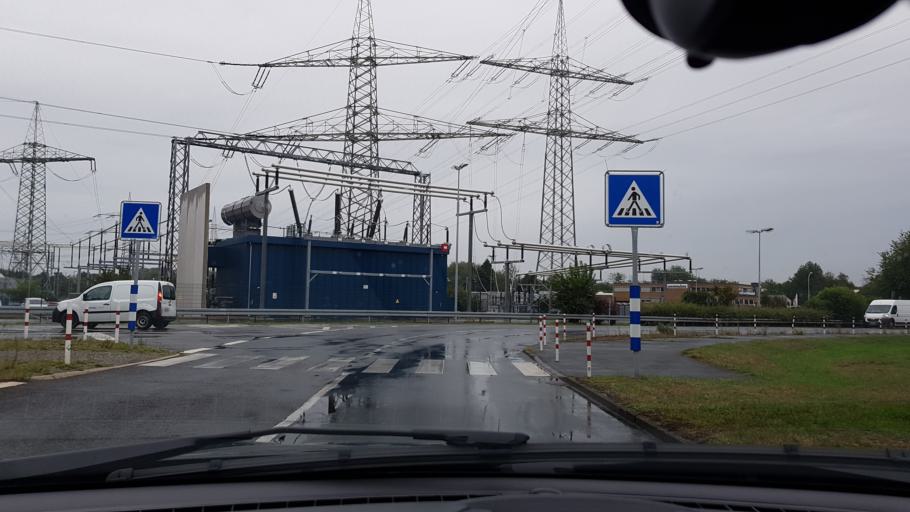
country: DE
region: North Rhine-Westphalia
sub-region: Regierungsbezirk Dusseldorf
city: Rommerskirchen
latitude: 50.9912
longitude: 6.6712
